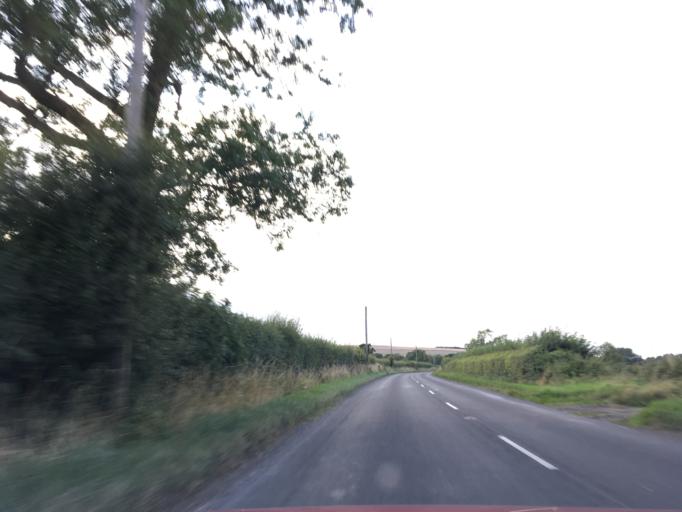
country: GB
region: England
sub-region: Wiltshire
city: Market Lavington
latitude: 51.3247
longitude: -1.9322
